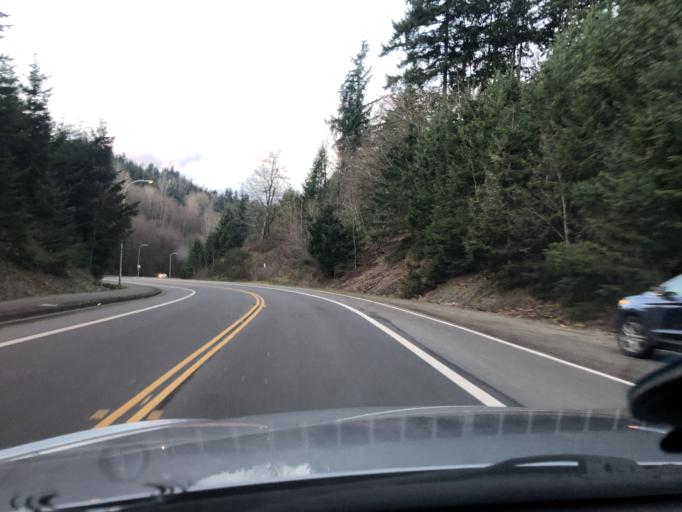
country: US
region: Washington
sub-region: King County
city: Lakeland North
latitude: 47.3171
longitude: -122.2557
